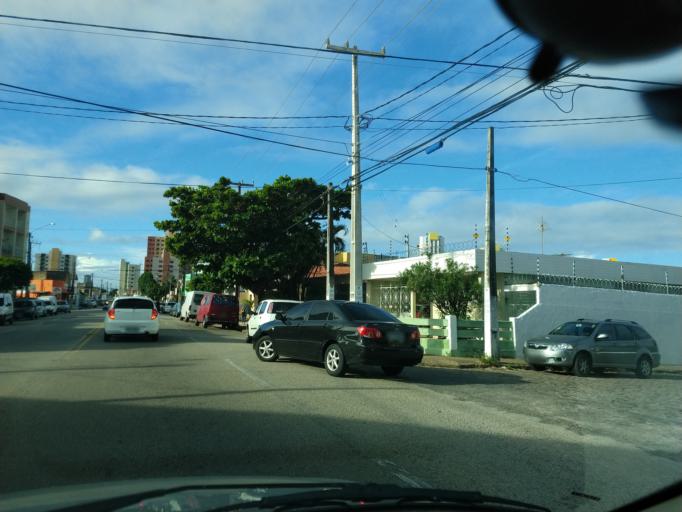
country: BR
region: Rio Grande do Norte
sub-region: Natal
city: Natal
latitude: -5.7995
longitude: -35.2113
